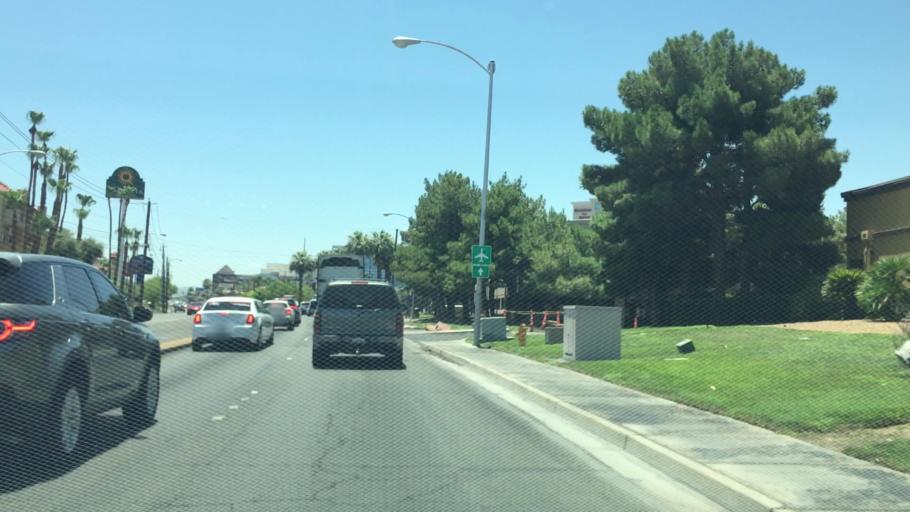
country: US
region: Nevada
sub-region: Clark County
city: Paradise
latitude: 36.1181
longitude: -115.1551
